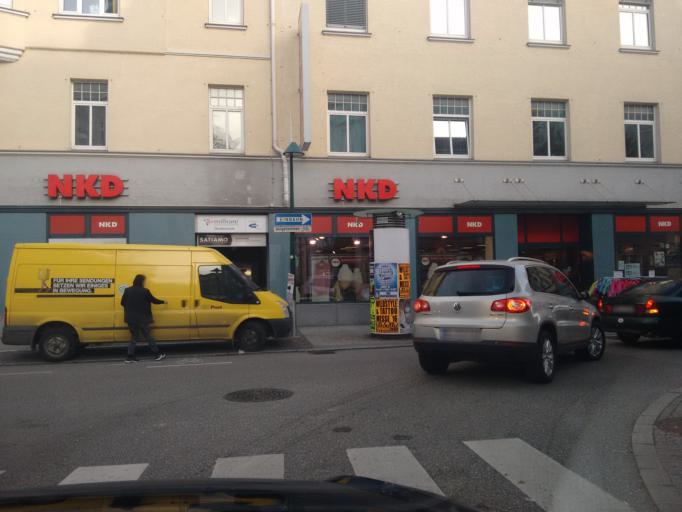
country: AT
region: Upper Austria
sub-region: Wels Stadt
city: Wels
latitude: 48.1616
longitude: 14.0250
